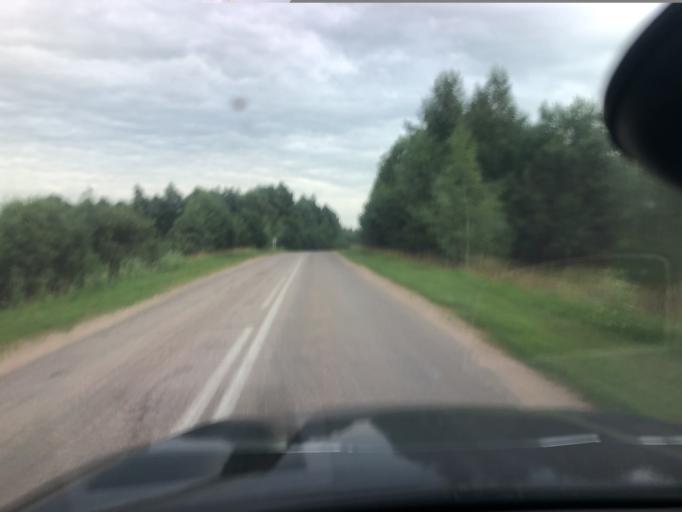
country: RU
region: Jaroslavl
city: Pereslavl'-Zalesskiy
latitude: 57.0124
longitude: 38.9659
